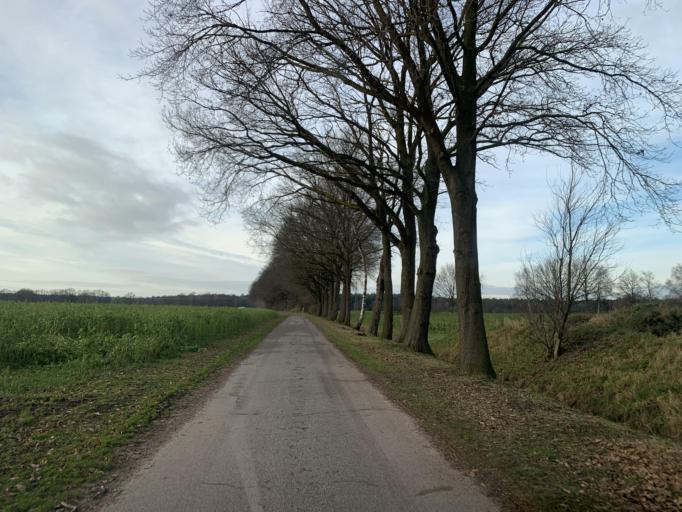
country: DE
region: North Rhine-Westphalia
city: Olfen
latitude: 51.7584
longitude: 7.3370
